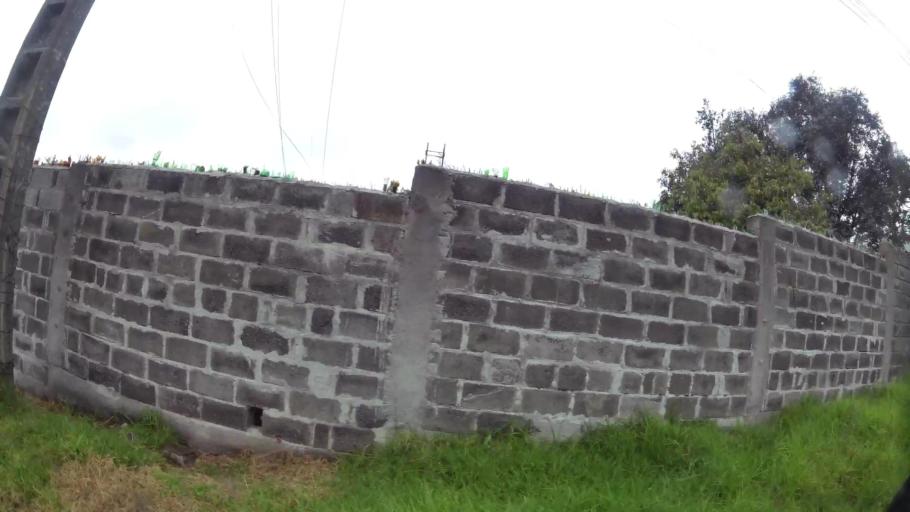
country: EC
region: Pichincha
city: Sangolqui
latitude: -0.2780
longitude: -78.4541
